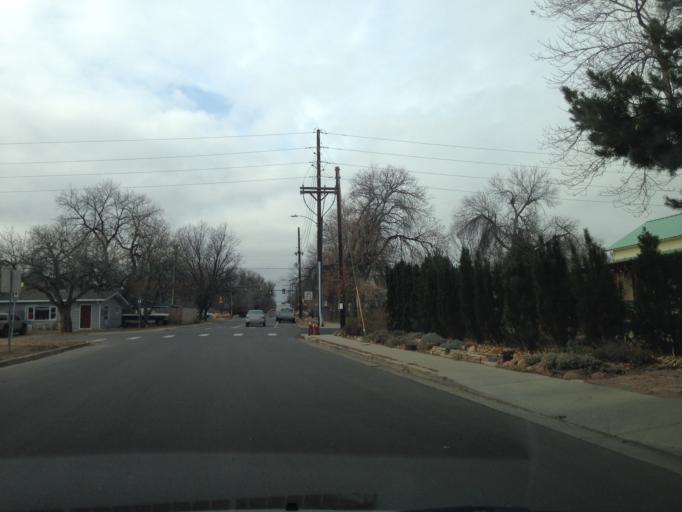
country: US
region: Colorado
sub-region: Boulder County
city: Lafayette
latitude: 39.9943
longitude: -105.0888
